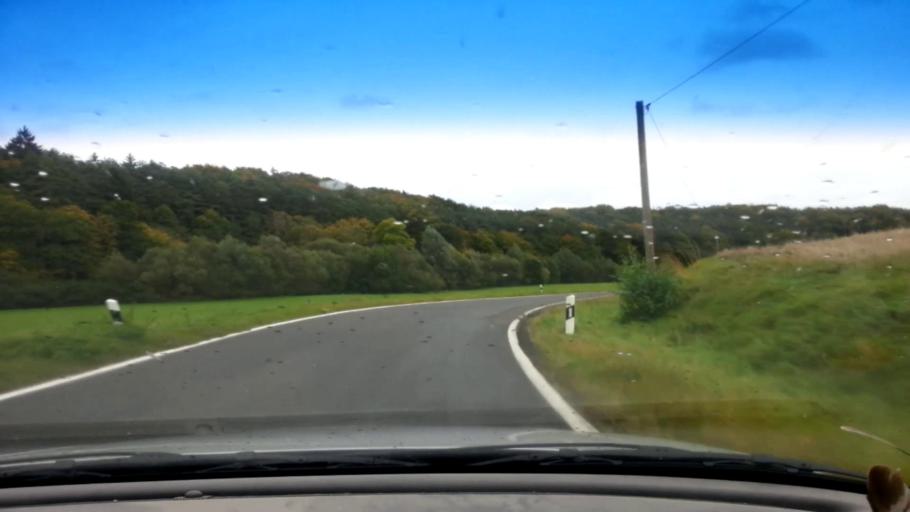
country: DE
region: Bavaria
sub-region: Regierungsbezirk Unterfranken
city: Kirchlauter
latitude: 50.0361
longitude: 10.7289
